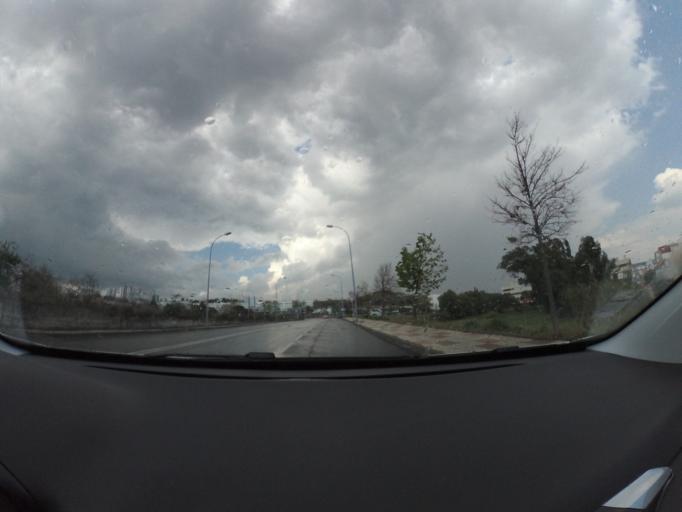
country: PT
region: Lisbon
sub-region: Oeiras
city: Linda-a-Velha
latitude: 38.7222
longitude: -9.2298
